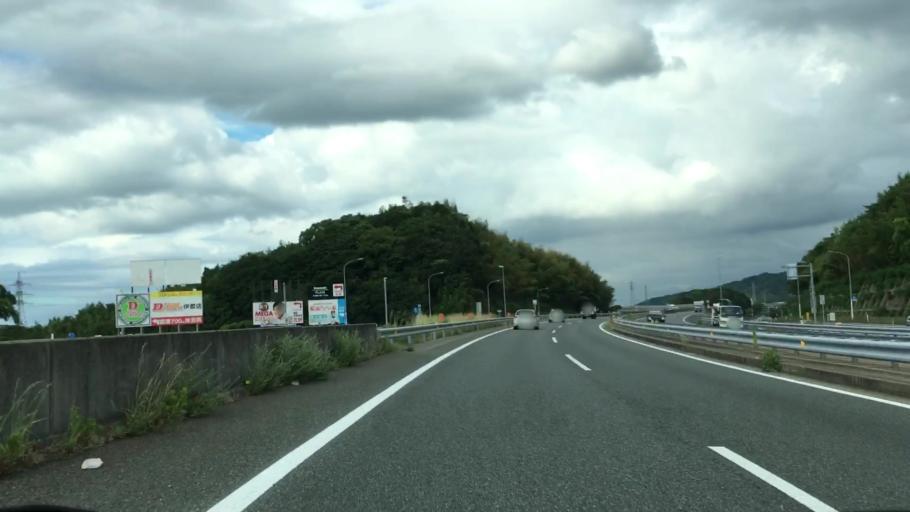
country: JP
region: Fukuoka
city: Maebaru-chuo
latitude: 33.5718
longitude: 130.2517
